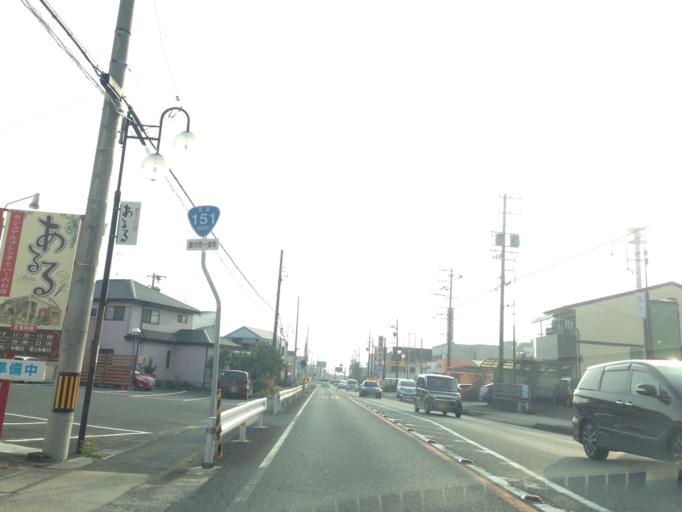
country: JP
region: Aichi
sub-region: Tokai-shi
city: Toyokawa
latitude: 34.8577
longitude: 137.4258
